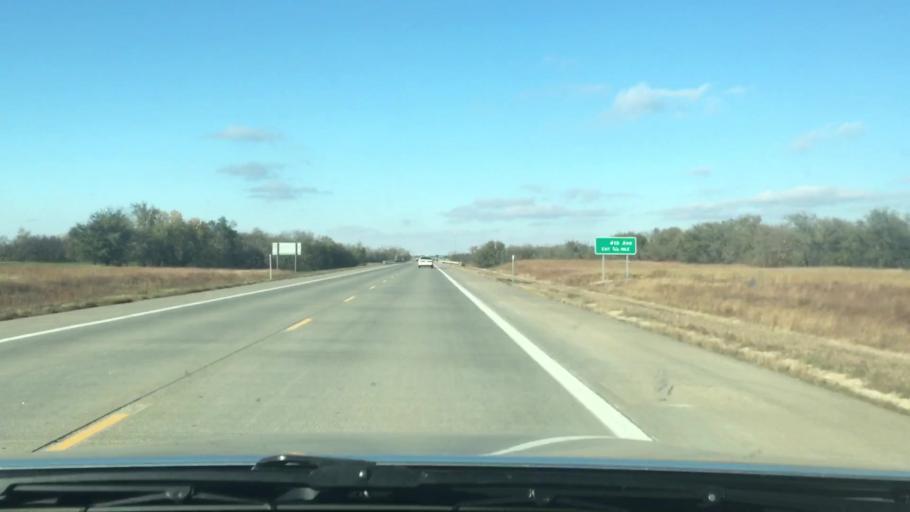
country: US
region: Kansas
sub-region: Reno County
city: South Hutchinson
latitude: 38.0443
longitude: -97.9858
